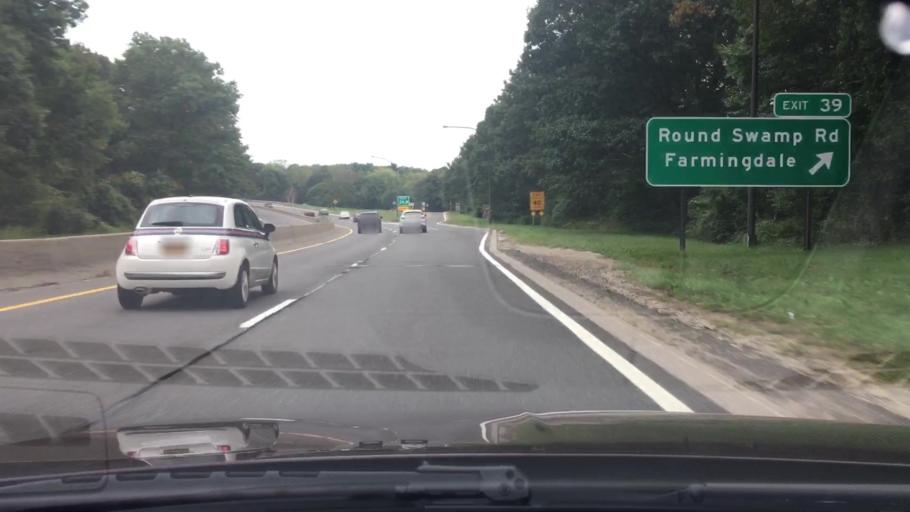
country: US
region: New York
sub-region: Suffolk County
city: West Hills
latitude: 40.8034
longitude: -73.4455
